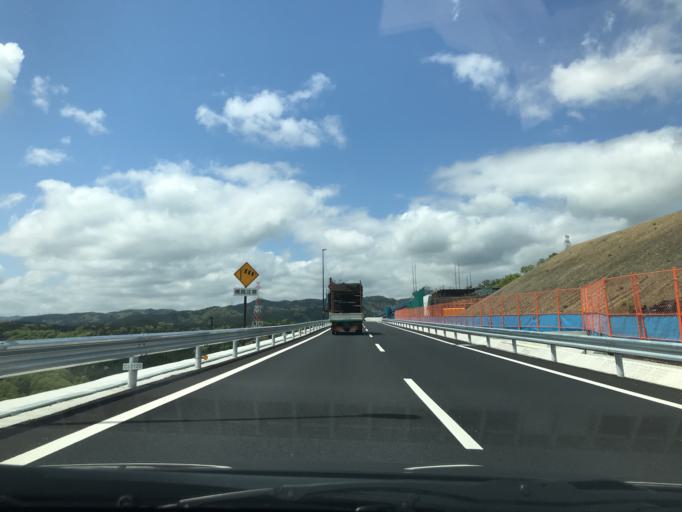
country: JP
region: Osaka
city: Takatsuki
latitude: 34.8839
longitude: 135.6199
